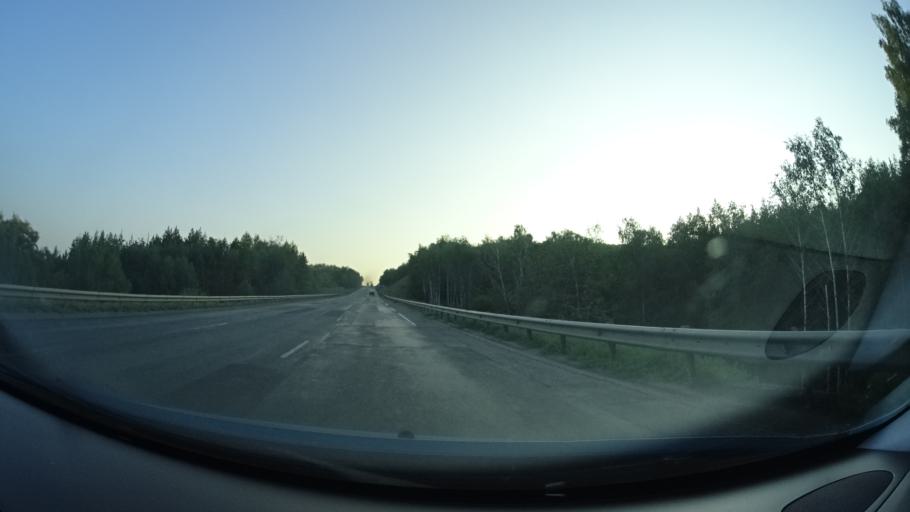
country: RU
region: Samara
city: Isakly
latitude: 53.9960
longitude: 51.5410
